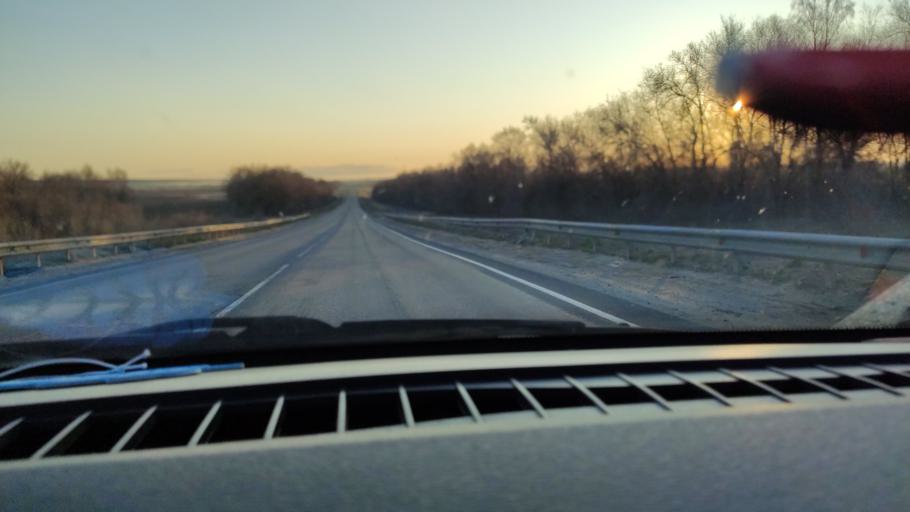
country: RU
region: Saratov
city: Sinodskoye
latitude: 51.9641
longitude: 46.6298
